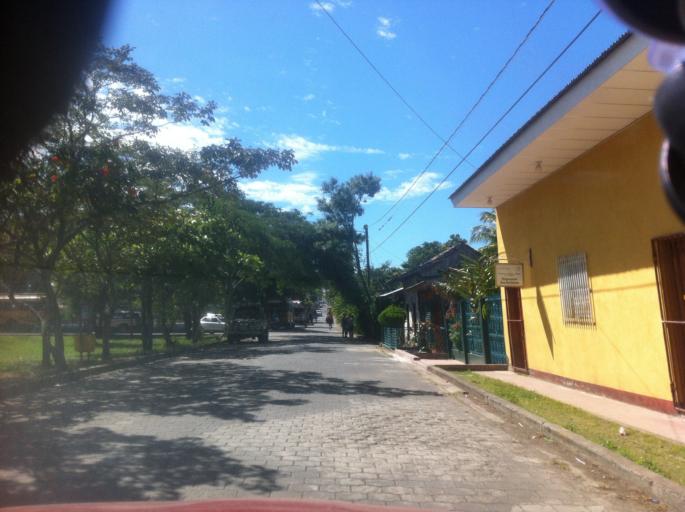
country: NI
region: Boaco
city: San Jose de los Remates
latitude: 12.6674
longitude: -85.7851
